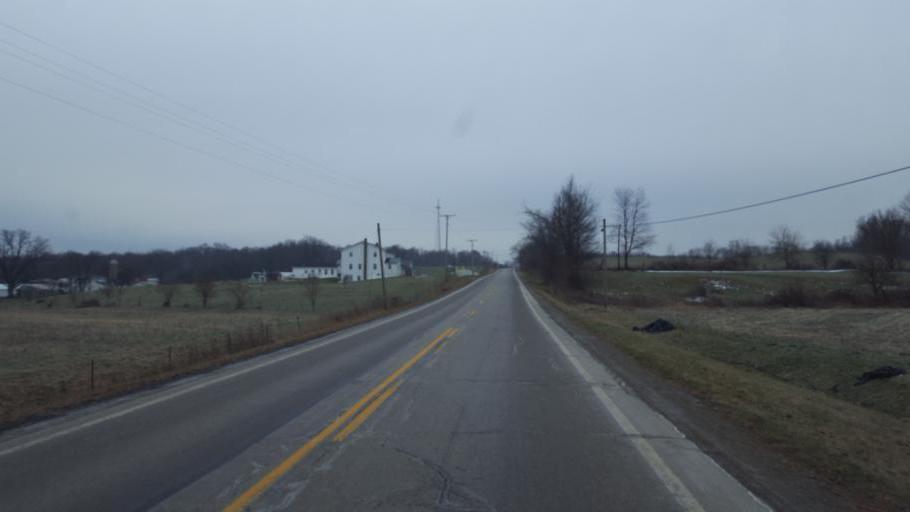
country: US
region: Ohio
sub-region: Knox County
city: Fredericktown
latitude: 40.5493
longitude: -82.6619
